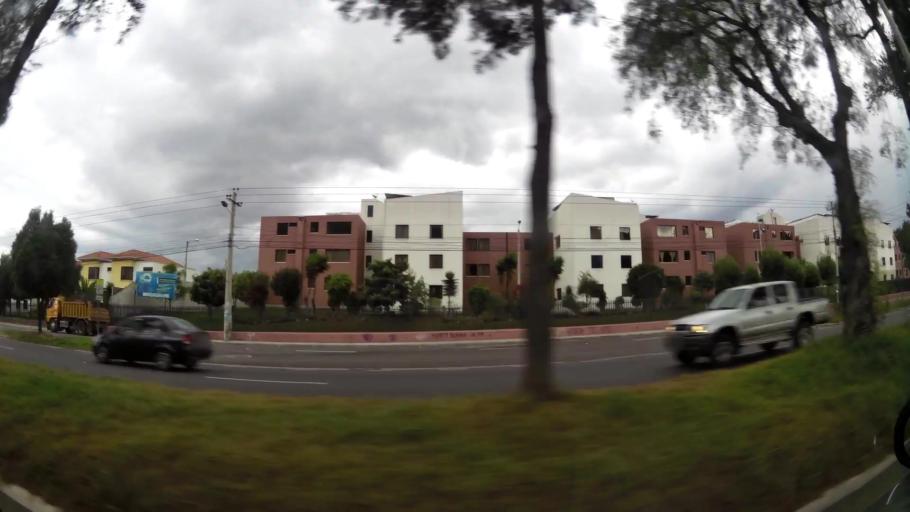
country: EC
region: Pichincha
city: Quito
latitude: -0.0685
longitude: -78.4687
